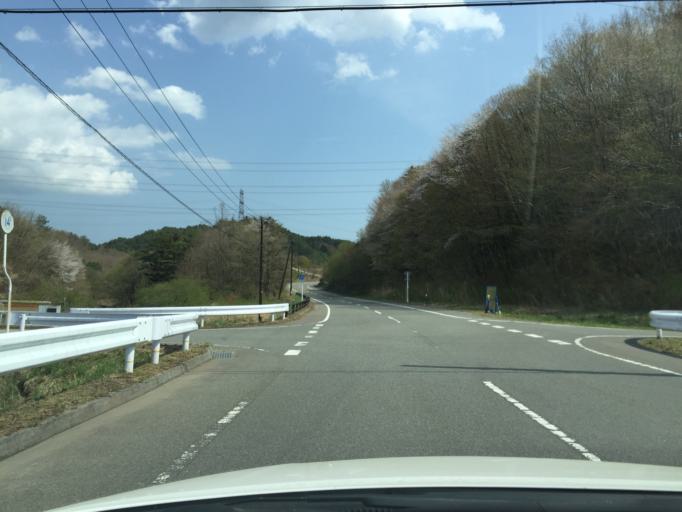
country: JP
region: Fukushima
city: Iwaki
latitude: 37.2877
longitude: 140.8402
